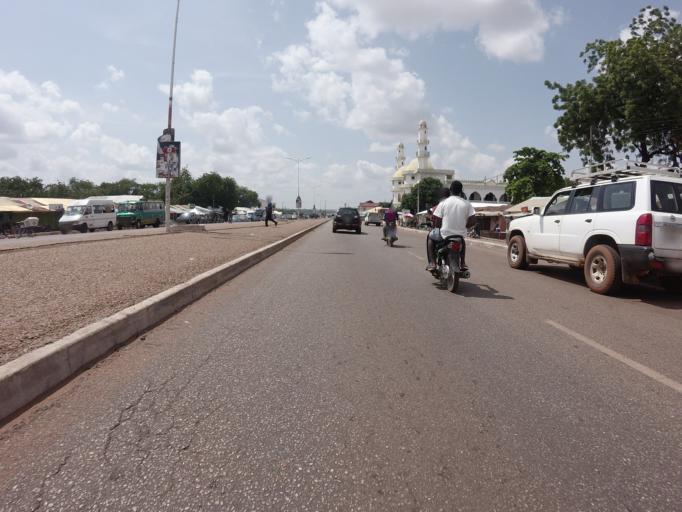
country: GH
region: Northern
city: Tamale
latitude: 9.4093
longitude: -0.8423
